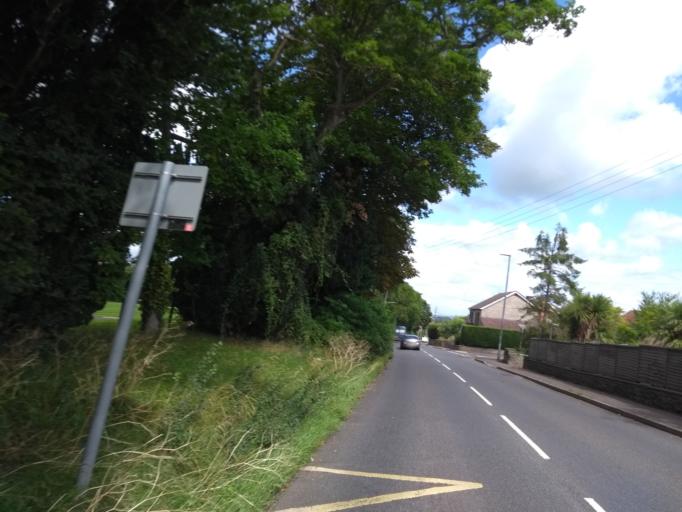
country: GB
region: England
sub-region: Somerset
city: Street
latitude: 51.1265
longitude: -2.7323
